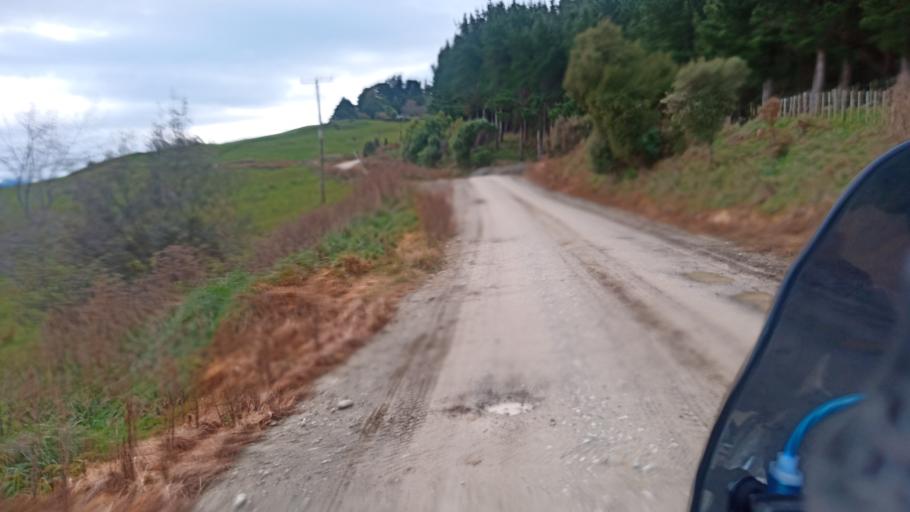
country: NZ
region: Gisborne
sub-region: Gisborne District
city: Gisborne
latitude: -38.3745
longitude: 177.9683
